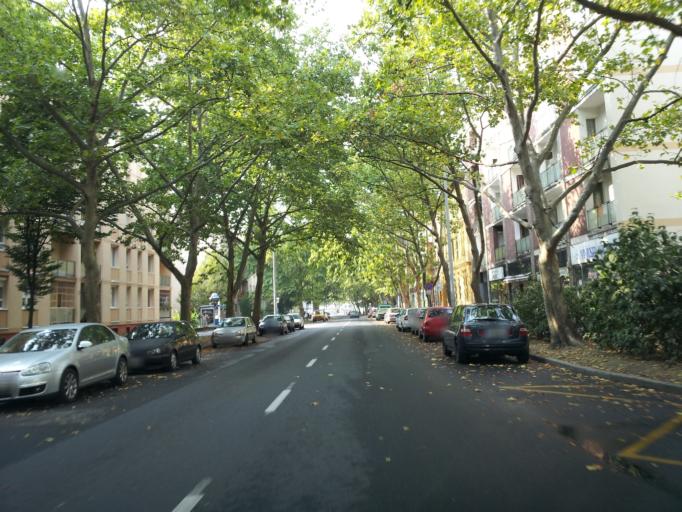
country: HU
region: Gyor-Moson-Sopron
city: Gyor
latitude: 47.6791
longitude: 17.6411
